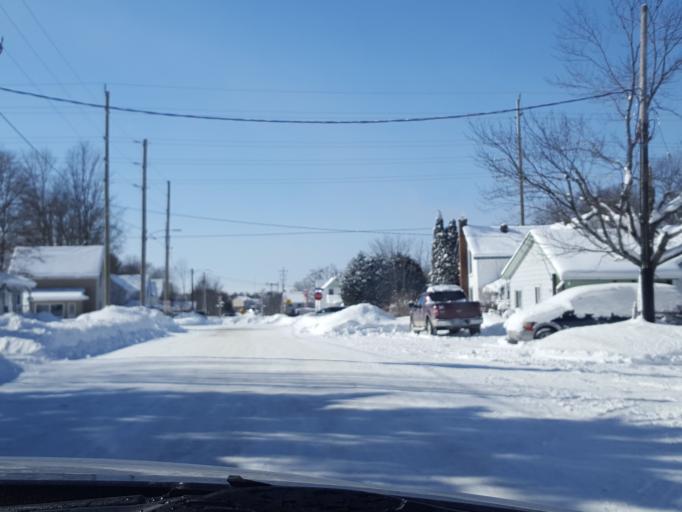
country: CA
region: Ontario
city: Gravenhurst
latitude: 44.9160
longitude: -79.3698
